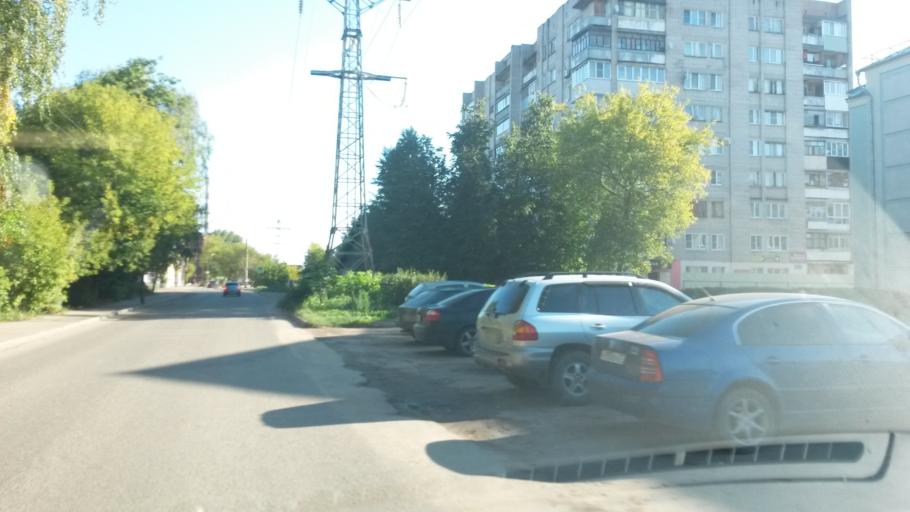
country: RU
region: Ivanovo
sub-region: Gorod Ivanovo
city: Ivanovo
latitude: 56.9991
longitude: 40.9597
